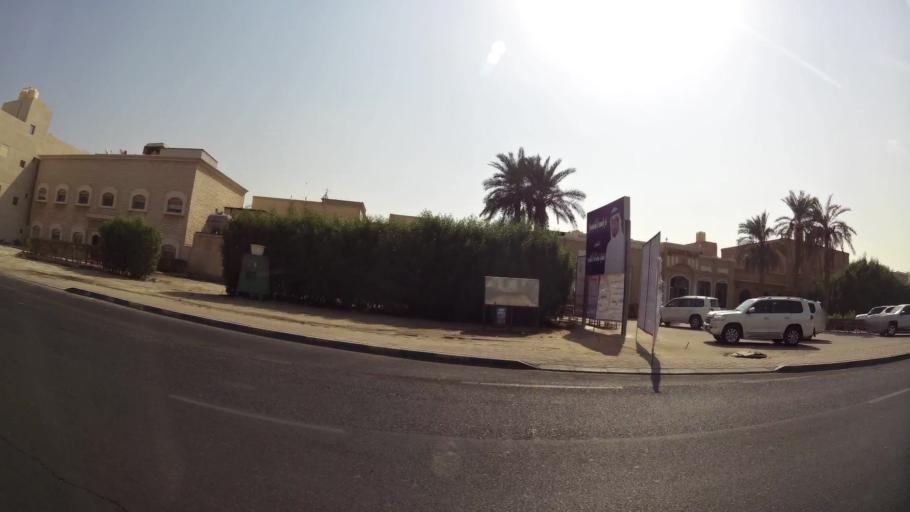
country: KW
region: Al Ahmadi
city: Al Manqaf
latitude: 29.0914
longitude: 48.1251
